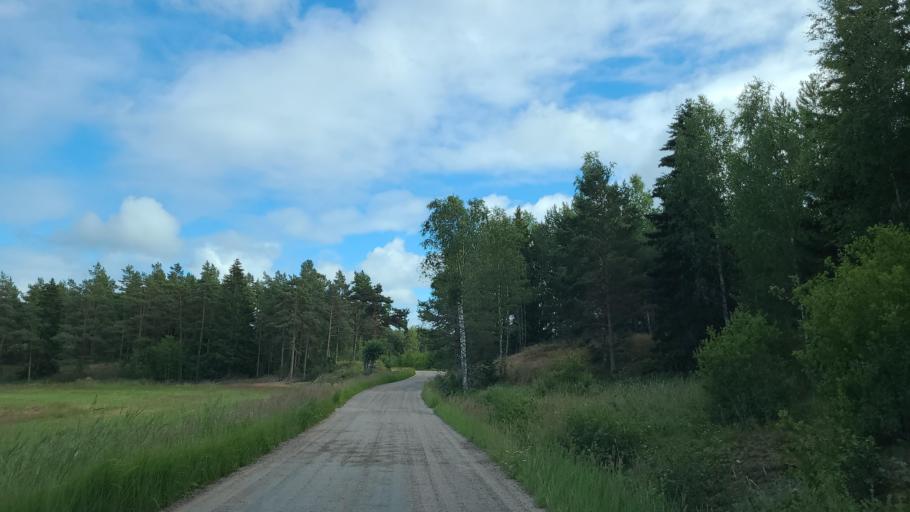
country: FI
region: Varsinais-Suomi
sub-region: Aboland-Turunmaa
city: Nagu
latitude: 60.1464
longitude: 21.7791
